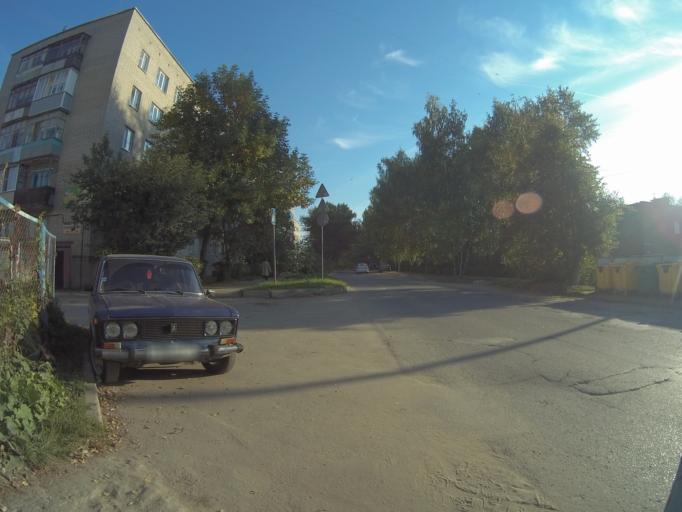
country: RU
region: Vladimir
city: Vladimir
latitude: 56.1117
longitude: 40.3735
